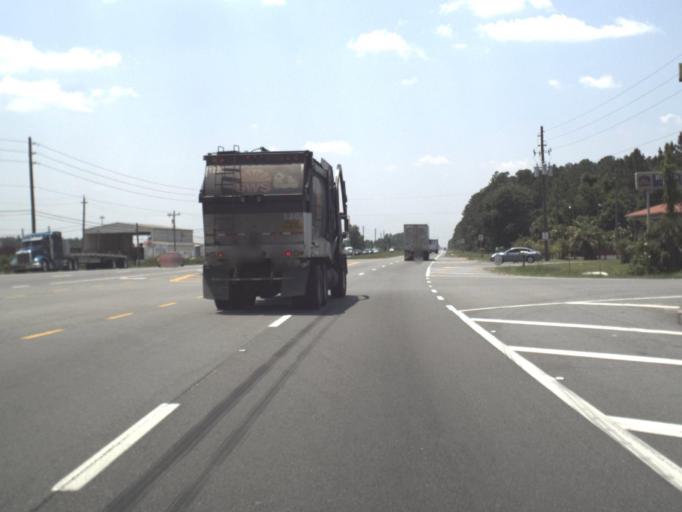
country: US
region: Florida
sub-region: Duval County
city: Baldwin
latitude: 30.2839
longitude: -81.9832
